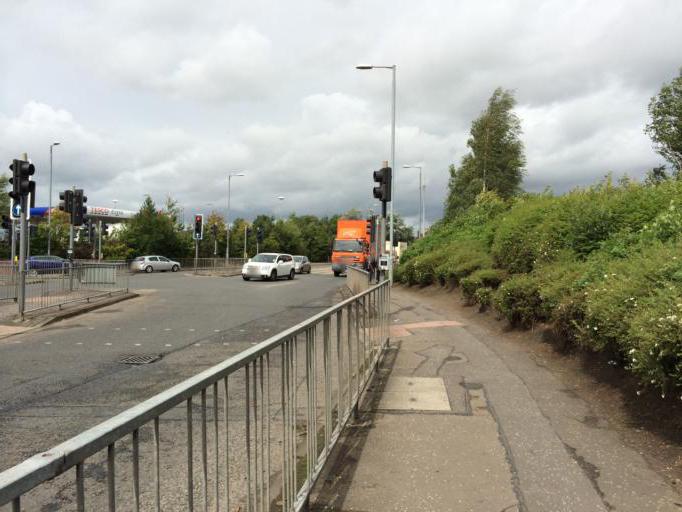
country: GB
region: Scotland
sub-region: North Lanarkshire
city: Stepps
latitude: 55.8520
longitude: -4.1602
